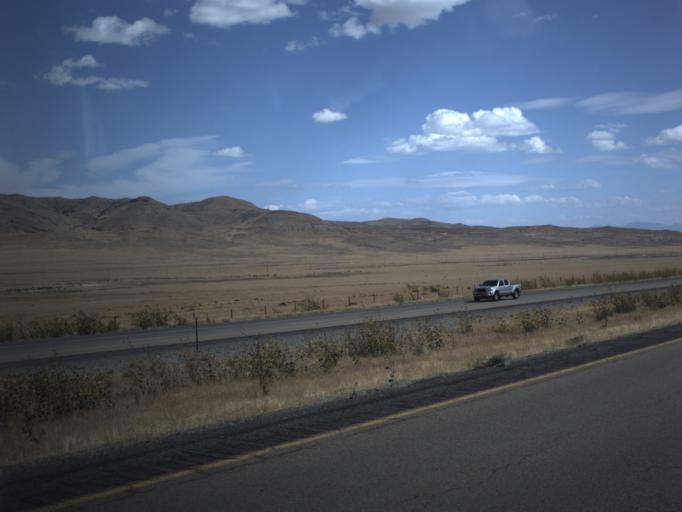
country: US
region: Utah
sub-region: Tooele County
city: Grantsville
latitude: 40.8157
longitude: -112.8784
